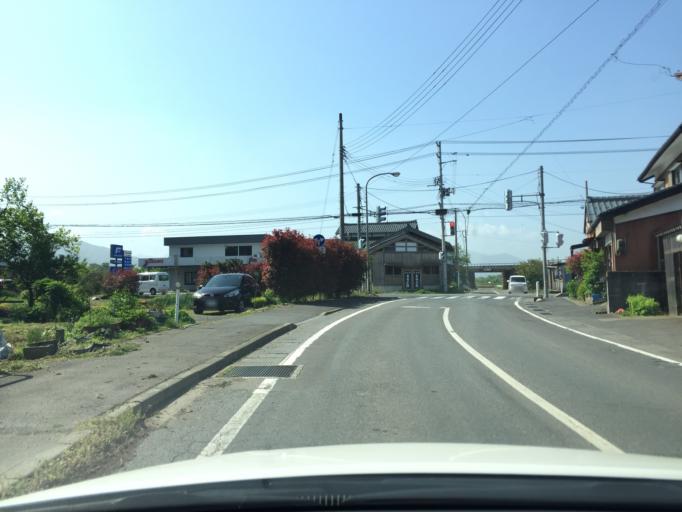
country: JP
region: Niigata
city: Gosen
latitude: 37.7320
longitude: 139.2072
